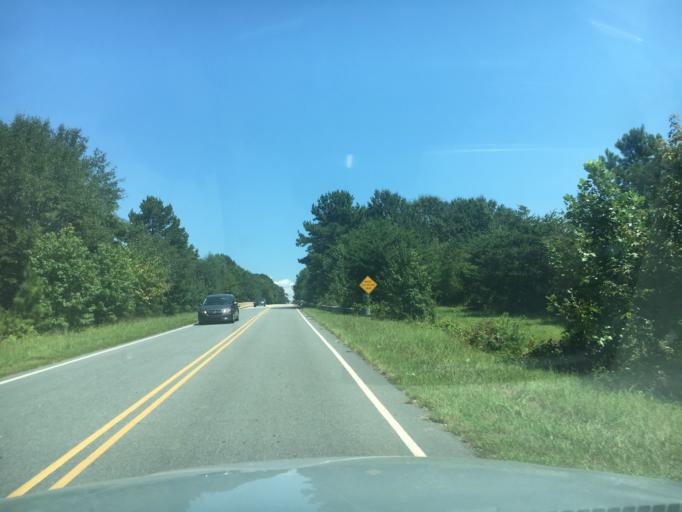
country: US
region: North Carolina
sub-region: Rutherford County
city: Forest City
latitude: 35.3096
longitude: -81.8886
